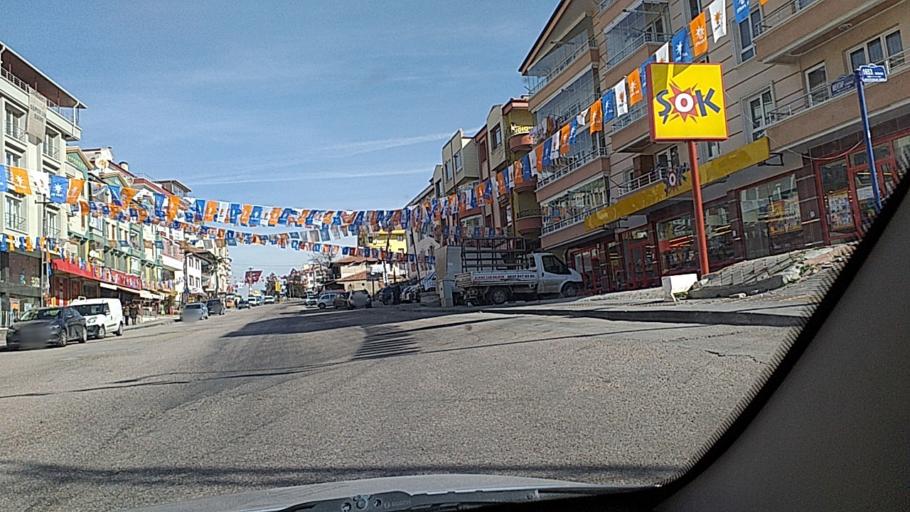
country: TR
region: Ankara
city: Batikent
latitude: 39.9934
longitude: 32.8106
